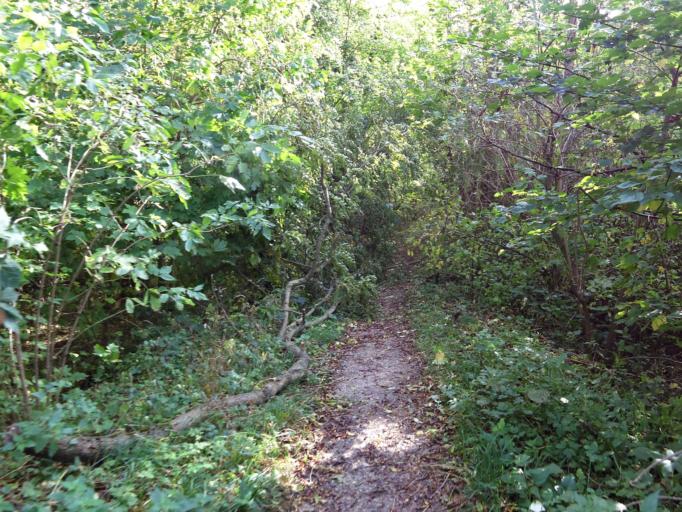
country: DE
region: Saxony
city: Leipzig
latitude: 51.3093
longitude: 12.3470
